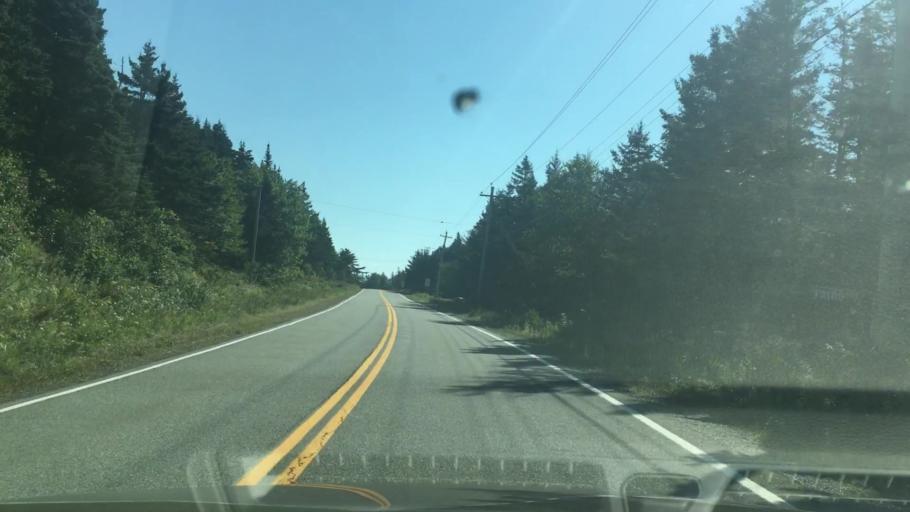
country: CA
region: Nova Scotia
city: New Glasgow
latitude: 44.8038
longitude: -62.7031
